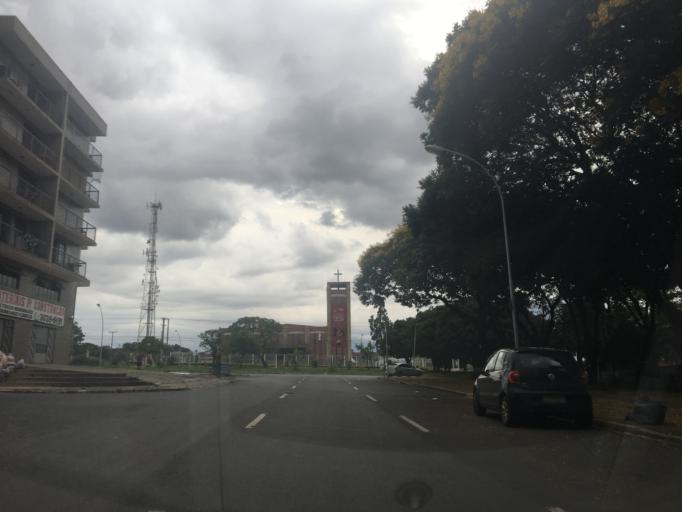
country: BR
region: Federal District
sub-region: Brasilia
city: Brasilia
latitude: -15.7449
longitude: -47.8993
